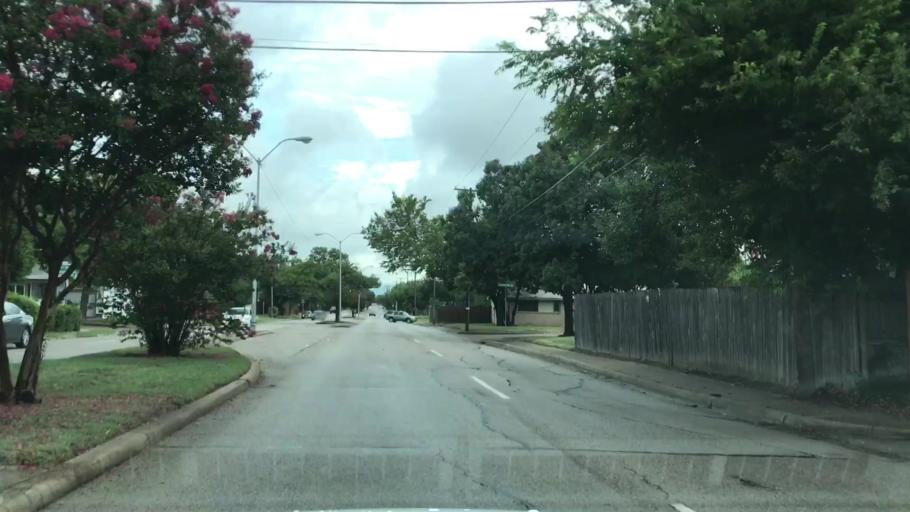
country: US
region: Texas
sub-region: Dallas County
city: Irving
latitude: 32.8484
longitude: -96.9765
